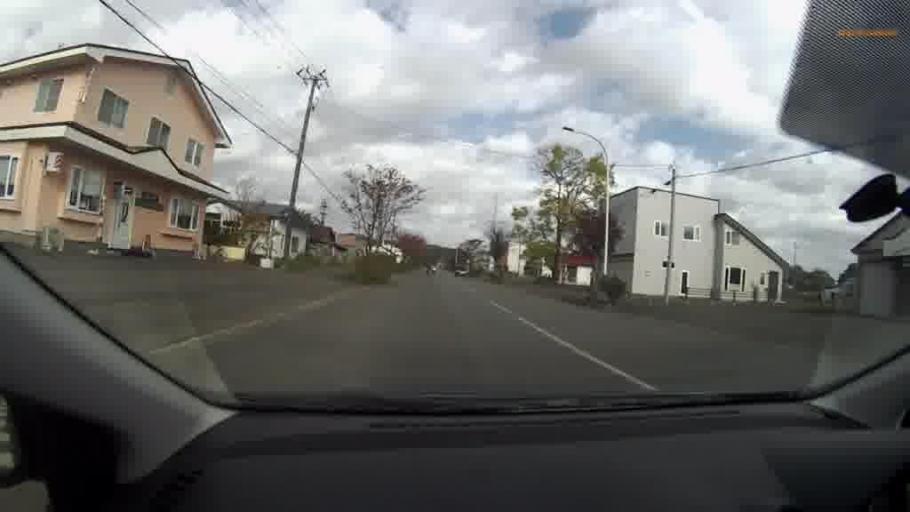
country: JP
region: Hokkaido
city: Kushiro
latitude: 42.9802
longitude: 144.1266
